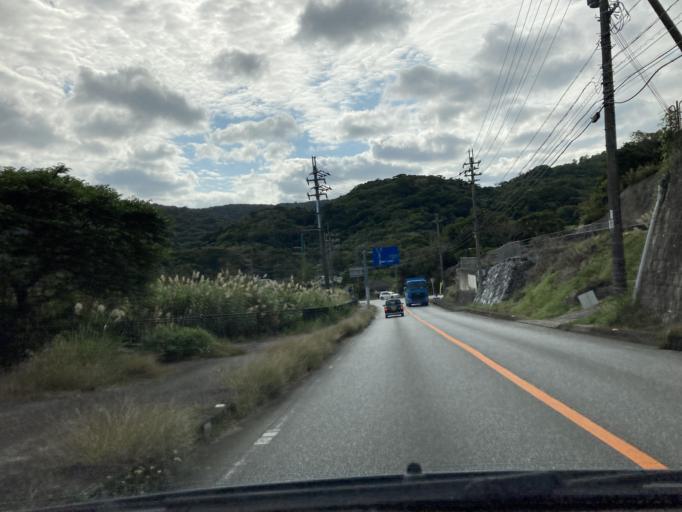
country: JP
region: Okinawa
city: Nago
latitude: 26.6544
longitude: 127.9824
